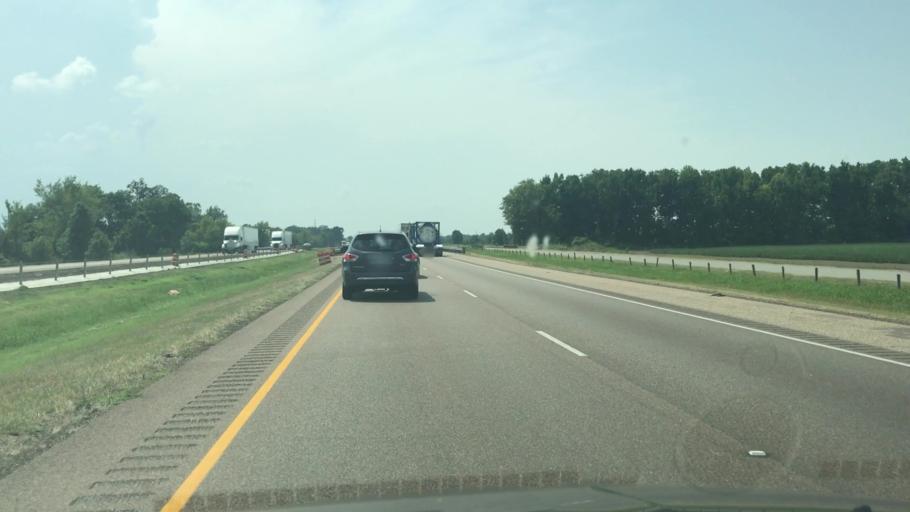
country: US
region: Arkansas
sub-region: Crittenden County
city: West Memphis
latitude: 35.1485
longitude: -90.3349
